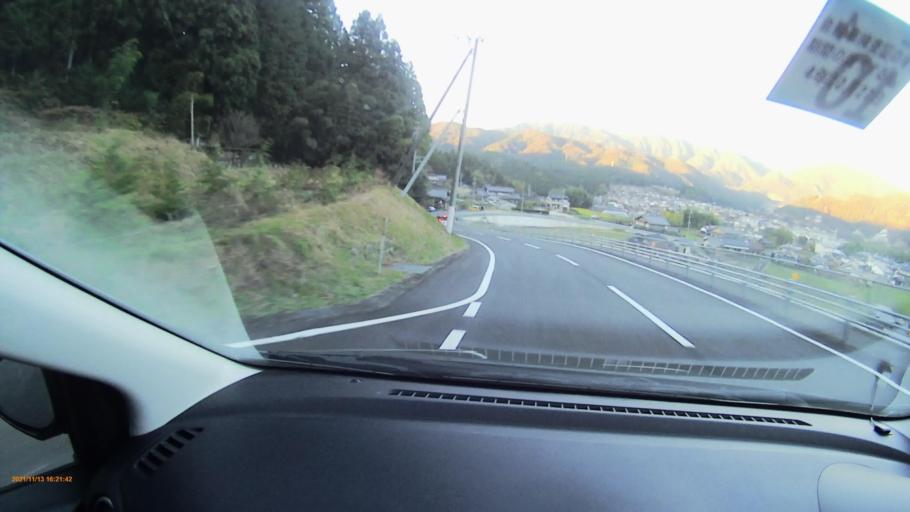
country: JP
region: Gifu
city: Nakatsugawa
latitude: 35.5682
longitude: 137.5240
